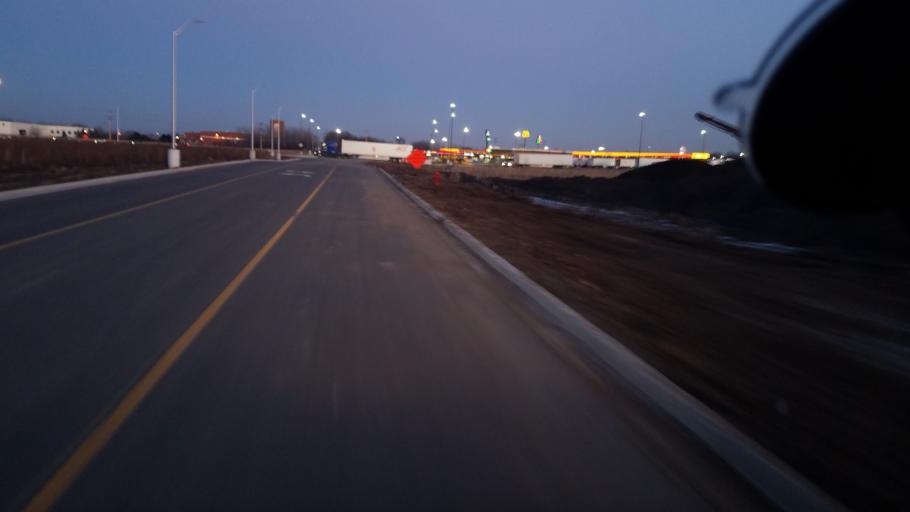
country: US
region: Illinois
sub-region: Kane County
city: Hampshire
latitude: 42.1500
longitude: -88.5179
